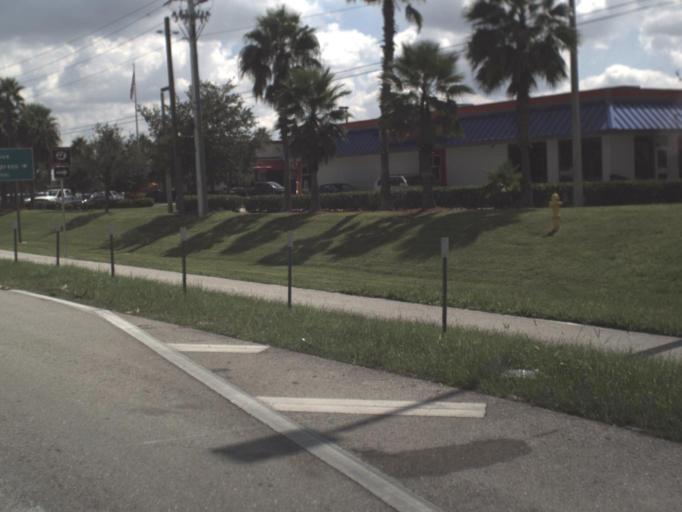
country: US
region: Florida
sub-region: Lee County
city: Fort Myers
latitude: 26.6125
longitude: -81.8148
